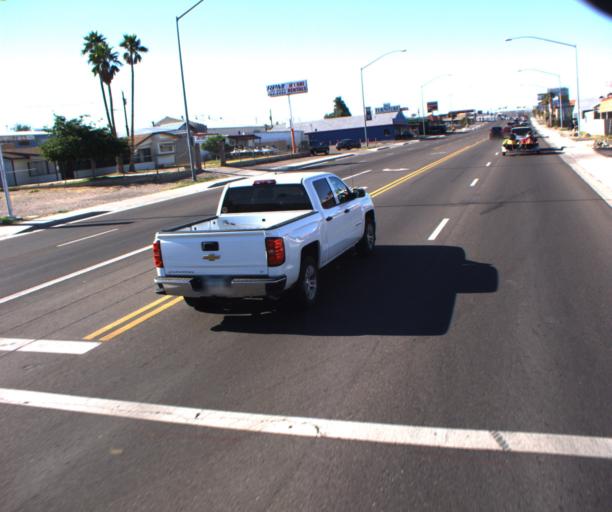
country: US
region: Arizona
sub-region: Mohave County
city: Bullhead City
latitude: 35.1531
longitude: -114.5676
